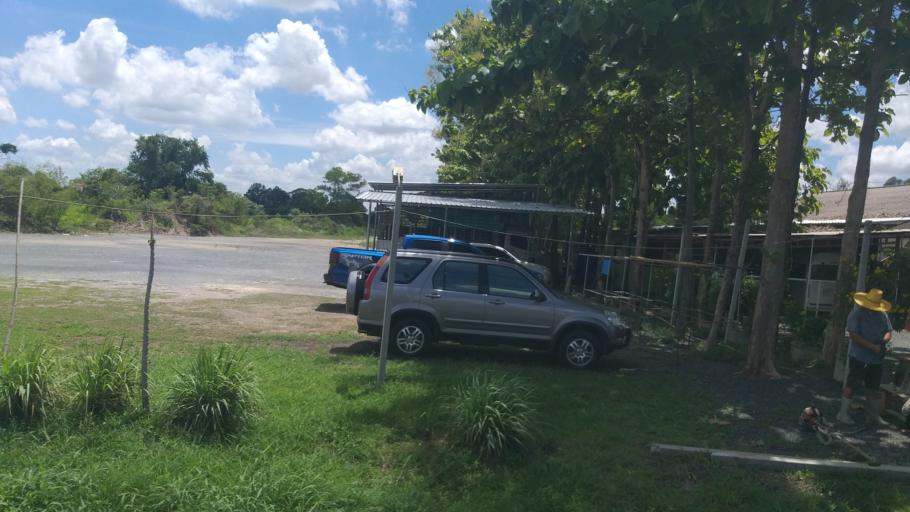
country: TH
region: Nakhon Nayok
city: Ban Na
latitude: 14.2739
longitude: 101.0660
